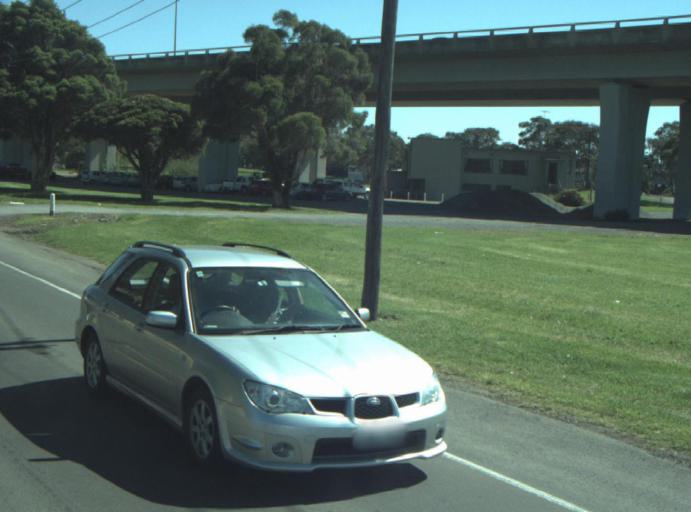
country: AU
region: Victoria
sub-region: Greater Geelong
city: Breakwater
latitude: -38.1671
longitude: 144.3505
